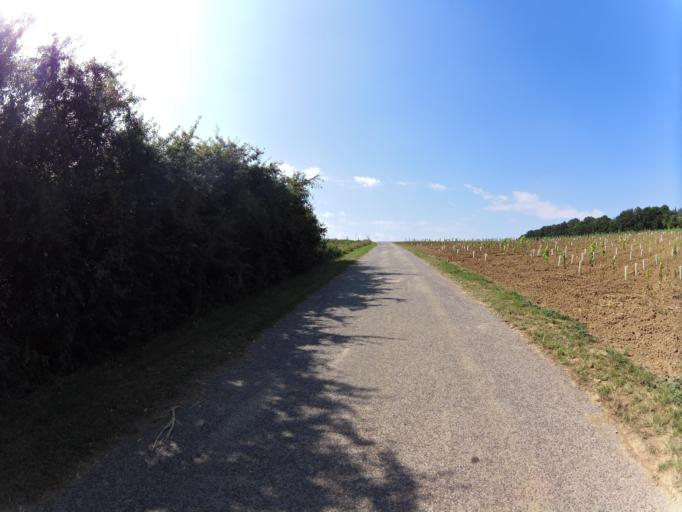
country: DE
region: Bavaria
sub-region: Regierungsbezirk Unterfranken
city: Nordheim
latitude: 49.8391
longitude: 10.1659
